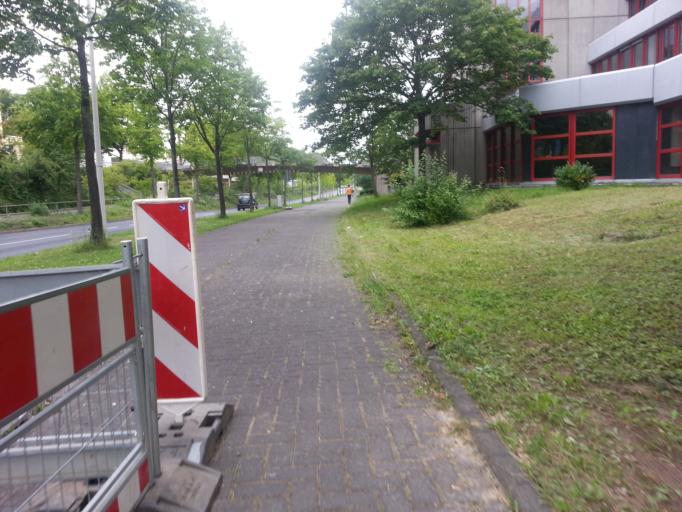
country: DE
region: North Rhine-Westphalia
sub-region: Regierungsbezirk Koln
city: Alfter
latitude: 50.7502
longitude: 7.0444
